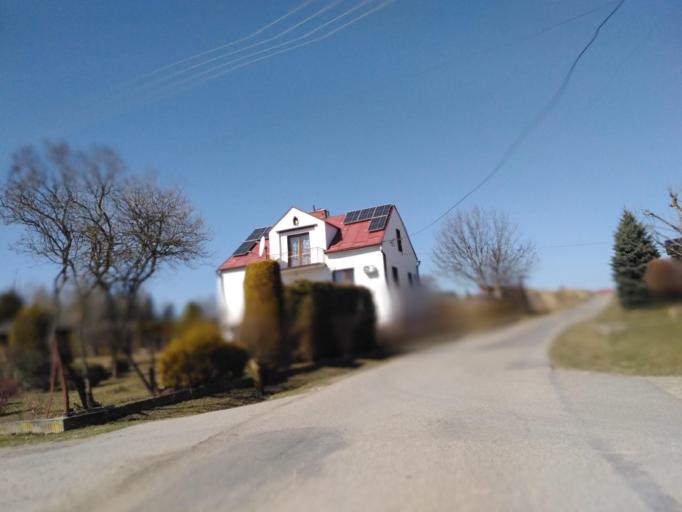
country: PL
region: Subcarpathian Voivodeship
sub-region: Powiat brzozowski
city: Orzechowka
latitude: 49.7149
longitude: 21.9656
